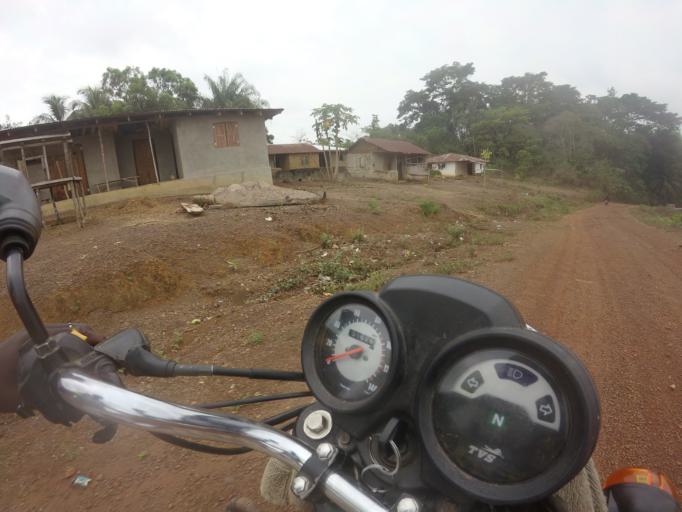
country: SL
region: Southern Province
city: Zimmi
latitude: 7.2075
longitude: -11.2057
